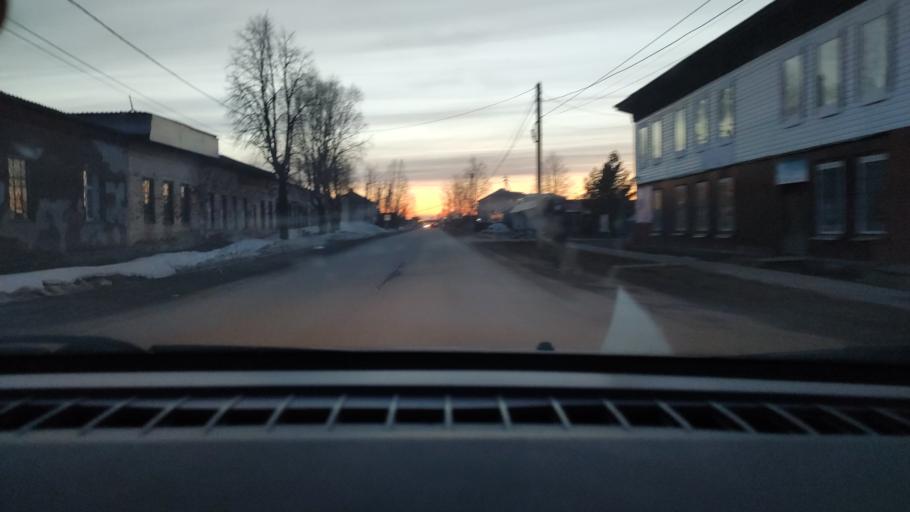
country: RU
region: Perm
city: Yug
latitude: 57.7322
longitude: 56.1764
